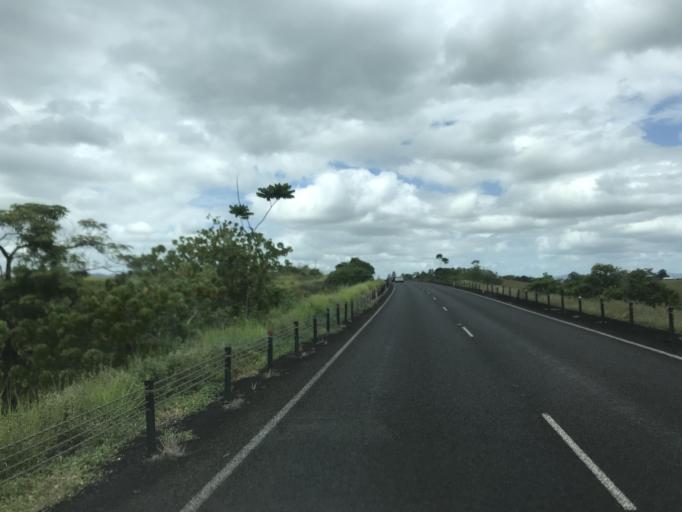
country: AU
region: Queensland
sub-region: Cassowary Coast
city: Innisfail
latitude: -17.5780
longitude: 145.9727
